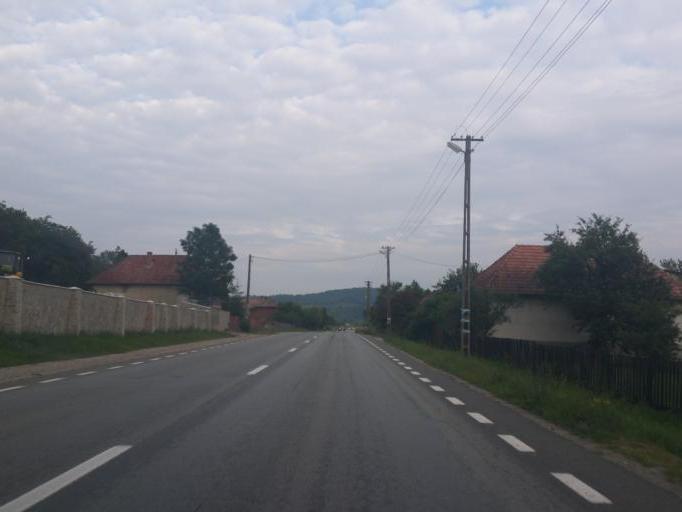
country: RO
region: Salaj
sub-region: Comuna Dragu
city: Dragu
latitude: 46.9532
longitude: 23.3516
